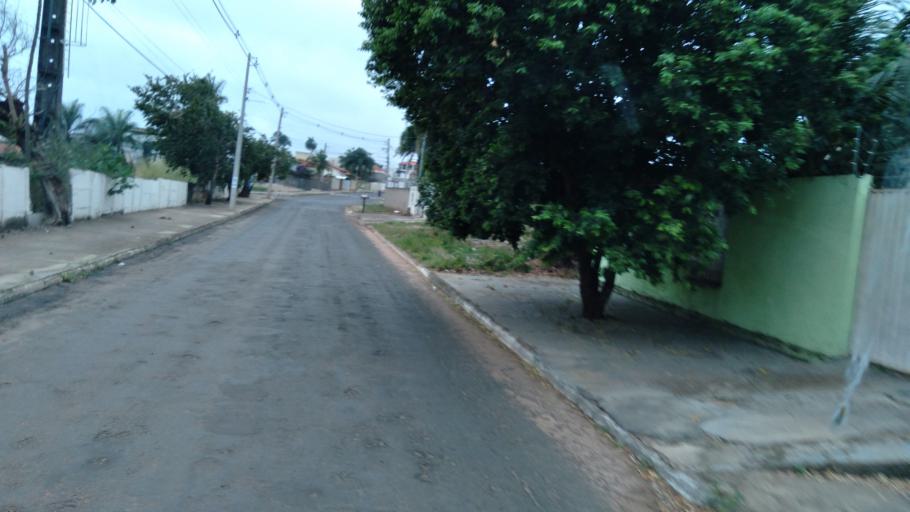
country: BR
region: Goias
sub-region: Mineiros
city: Mineiros
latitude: -17.5744
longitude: -52.5470
